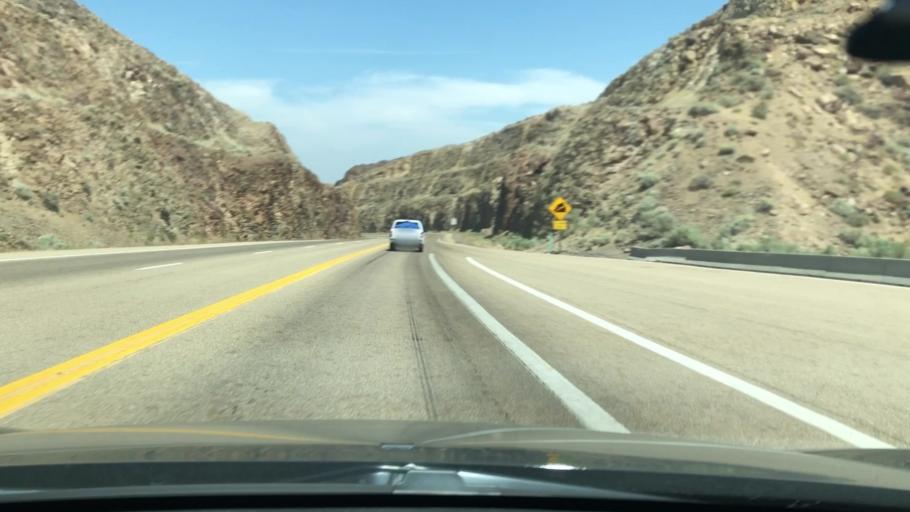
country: US
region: Idaho
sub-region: Owyhee County
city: Marsing
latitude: 43.4090
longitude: -116.8643
